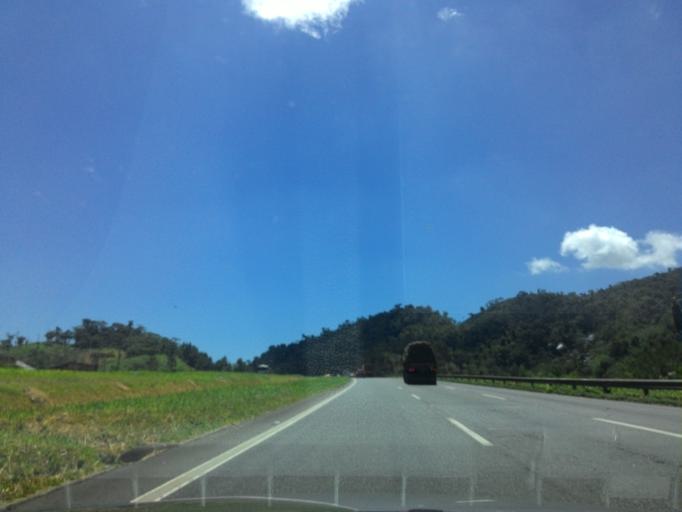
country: BR
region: Parana
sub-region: Antonina
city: Antonina
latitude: -25.0113
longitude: -48.5078
